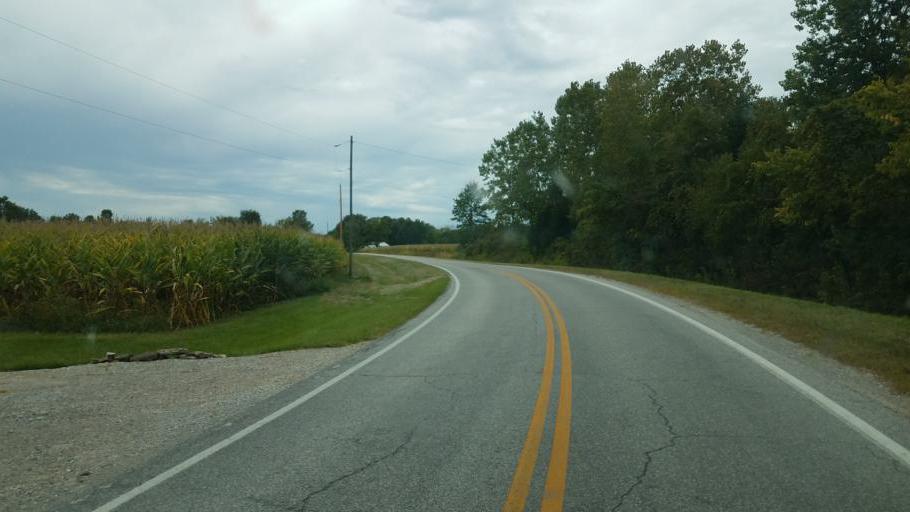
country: US
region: Ohio
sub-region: Delaware County
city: Sunbury
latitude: 40.2630
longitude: -82.8123
